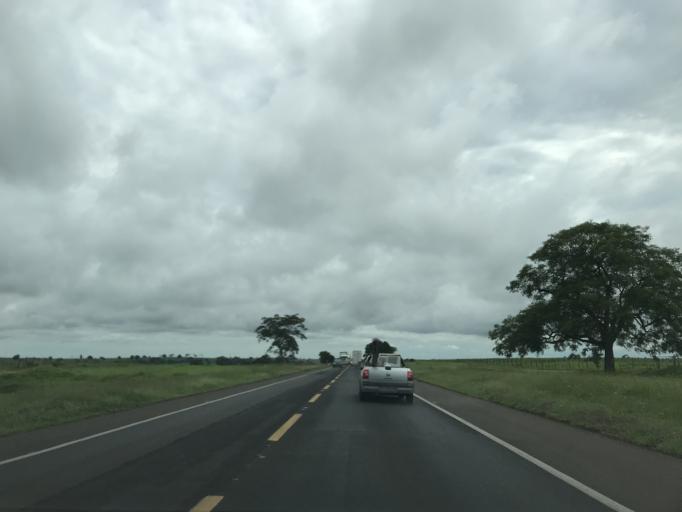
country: BR
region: Sao Paulo
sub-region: Nova Granada
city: Nova Granada
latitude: -20.4873
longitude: -49.3067
